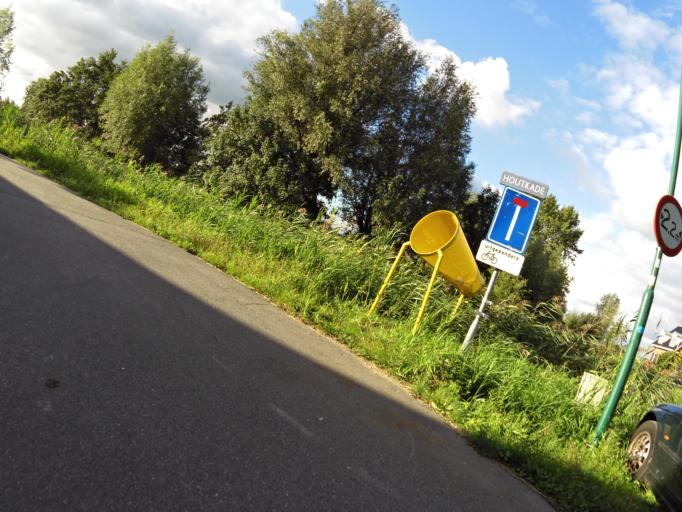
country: NL
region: Utrecht
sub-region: Gemeente Woerden
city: Woerden
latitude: 52.1391
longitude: 4.8930
